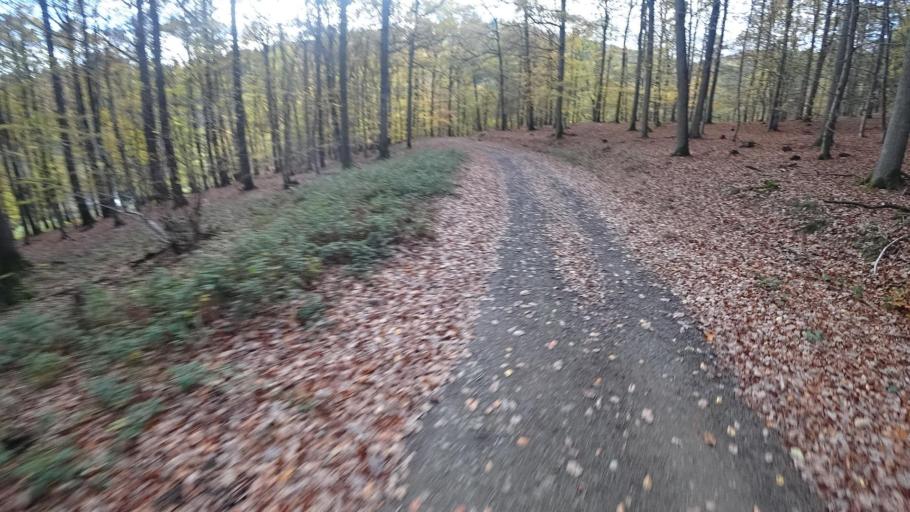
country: DE
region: Rheinland-Pfalz
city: Honningen
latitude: 50.4828
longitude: 6.9490
